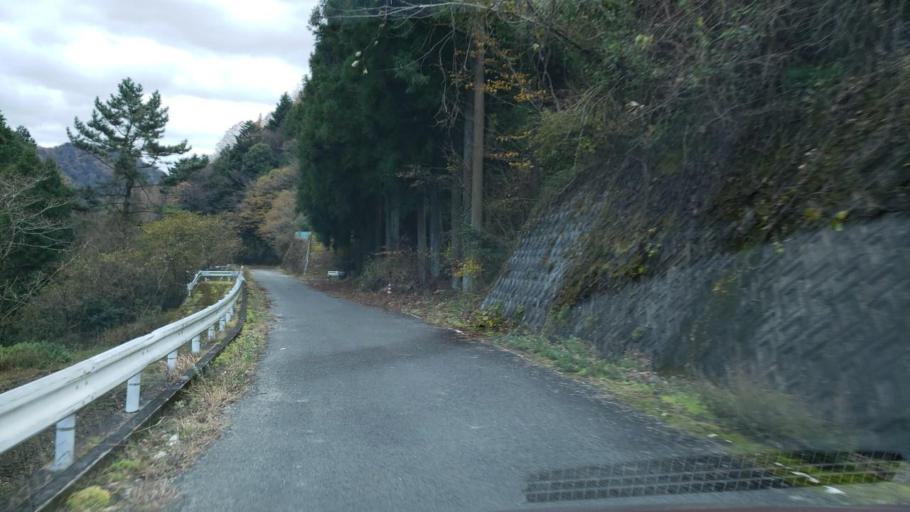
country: JP
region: Tokushima
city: Wakimachi
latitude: 34.1478
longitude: 134.2278
